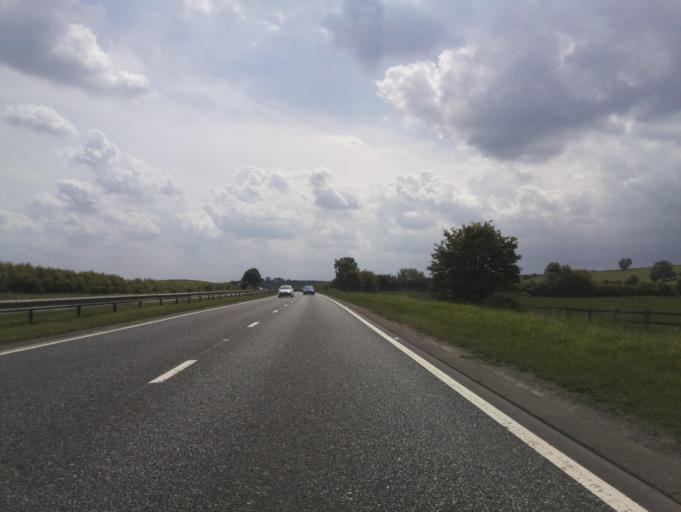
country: GB
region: England
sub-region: North Yorkshire
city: Thirsk
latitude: 54.3258
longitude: -1.3384
